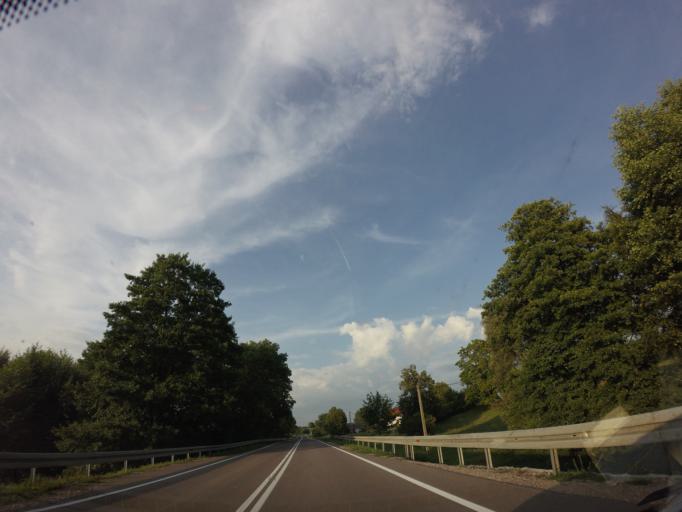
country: LT
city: Lazdijai
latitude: 54.1324
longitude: 23.4603
